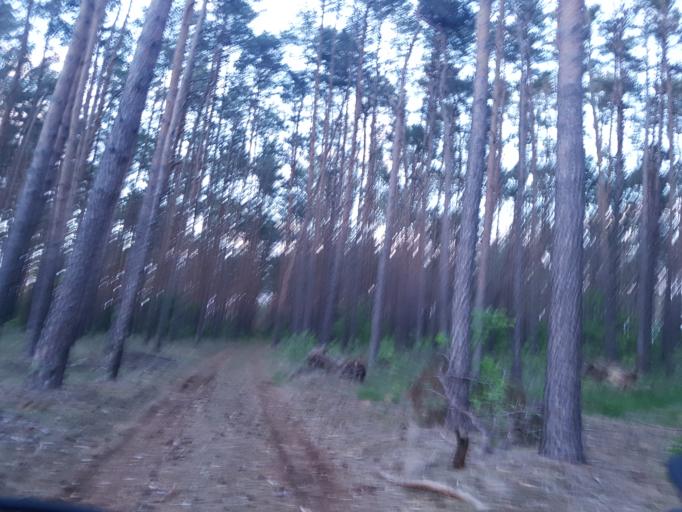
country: DE
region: Brandenburg
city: Schilda
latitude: 51.5637
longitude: 13.3745
